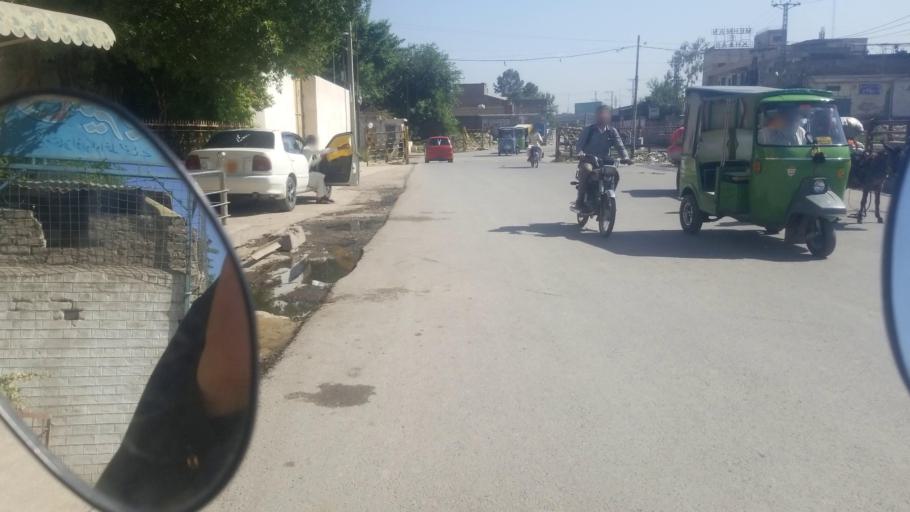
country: PK
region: Khyber Pakhtunkhwa
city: Peshawar
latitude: 34.0185
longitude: 71.5928
